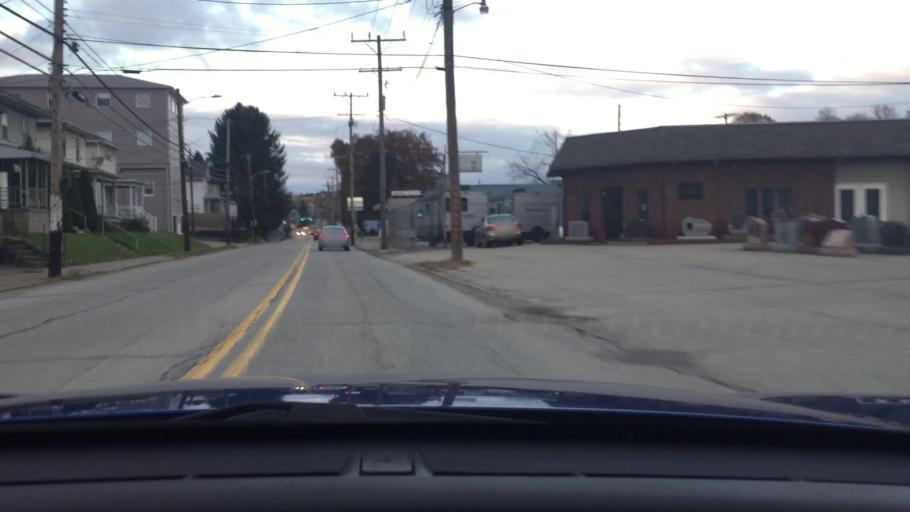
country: US
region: Pennsylvania
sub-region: Westmoreland County
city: Southwest Greensburg
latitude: 40.2925
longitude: -79.5439
